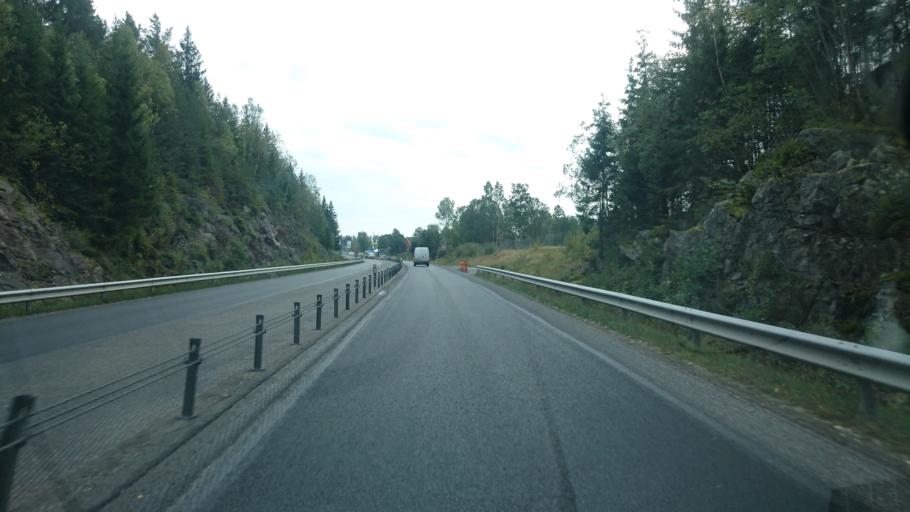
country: SE
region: Vaestra Goetaland
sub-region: Boras Kommun
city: Dalsjofors
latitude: 57.6197
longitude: 13.1055
